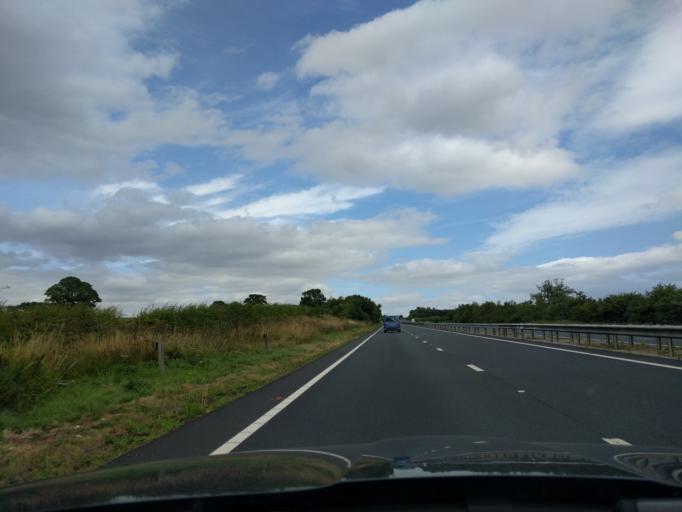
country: GB
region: England
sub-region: Northumberland
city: Felton
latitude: 55.3080
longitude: -1.7258
